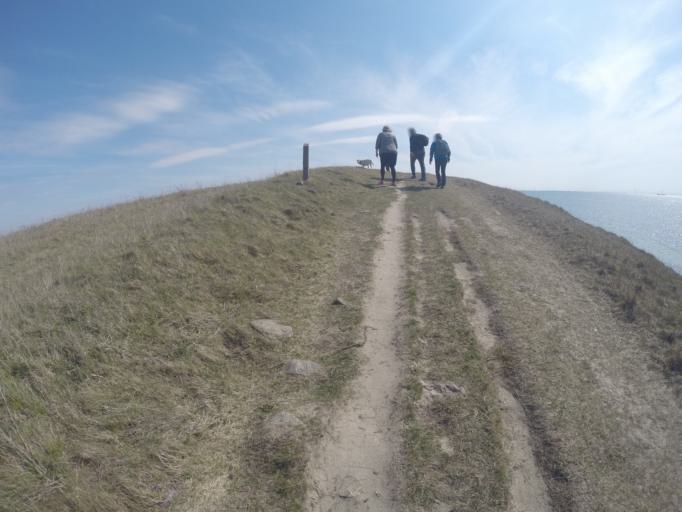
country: DK
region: Zealand
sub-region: Kalundborg Kommune
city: Gorlev
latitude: 55.5133
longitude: 11.0892
